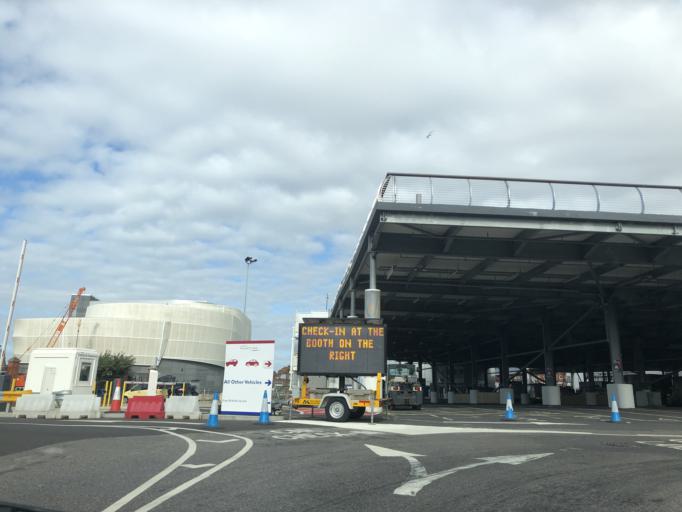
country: GB
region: England
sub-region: Portsmouth
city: Portsmouth
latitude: 50.7925
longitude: -1.1047
